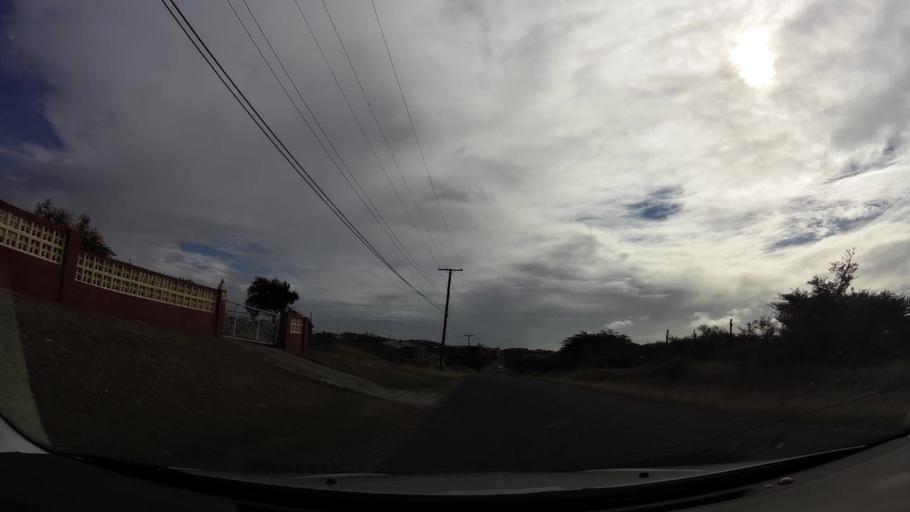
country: AG
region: Saint Peter
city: Parham
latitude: 17.0845
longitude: -61.7207
